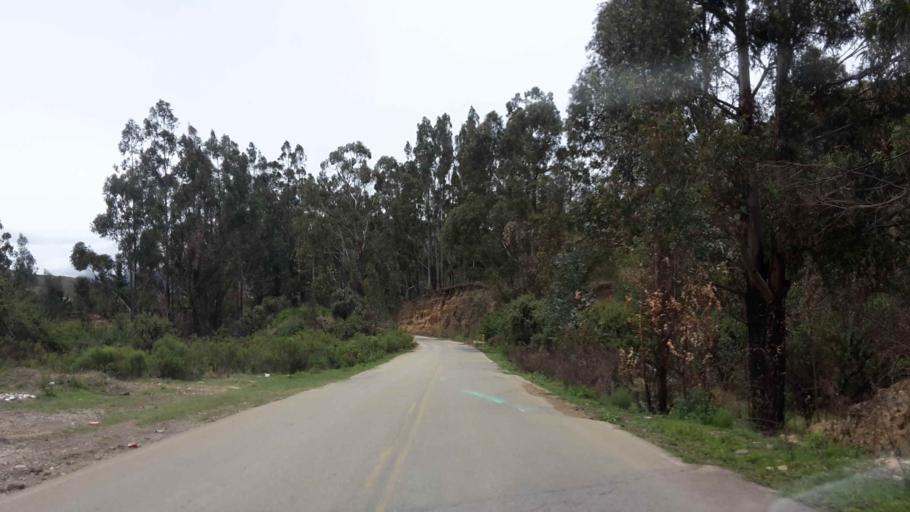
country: BO
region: Cochabamba
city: Totora
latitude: -17.6604
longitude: -65.2262
